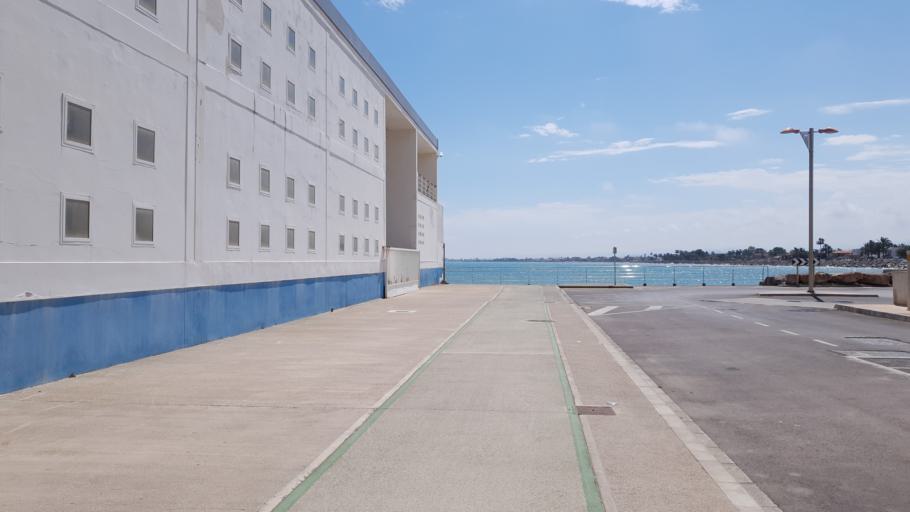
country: ES
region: Valencia
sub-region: Provincia de Castello
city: Burriana
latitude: 39.8627
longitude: -0.0760
